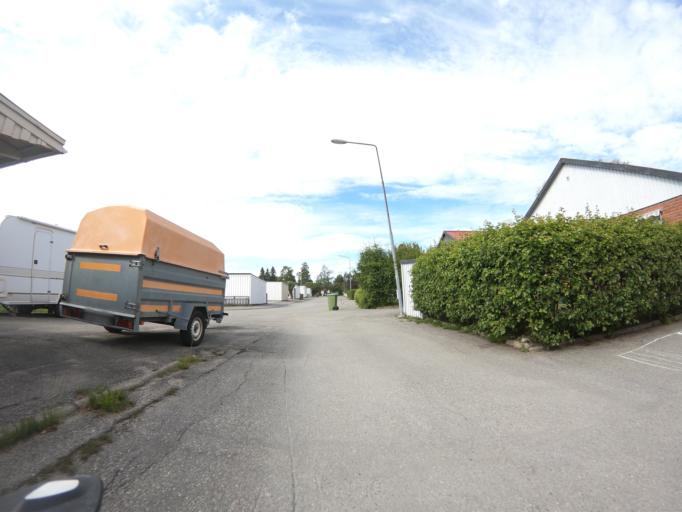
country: SE
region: Vaesterbotten
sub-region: Umea Kommun
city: Umea
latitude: 63.8165
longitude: 20.2614
